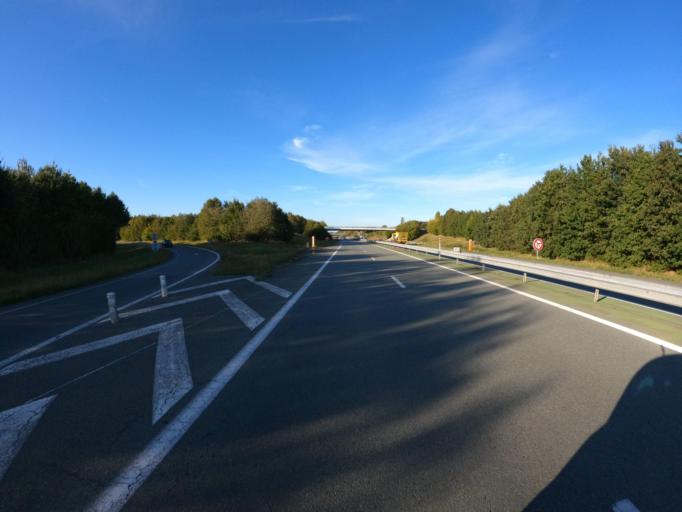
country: FR
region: Pays de la Loire
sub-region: Departement de Maine-et-Loire
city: Nuaille
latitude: 47.0851
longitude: -0.8244
